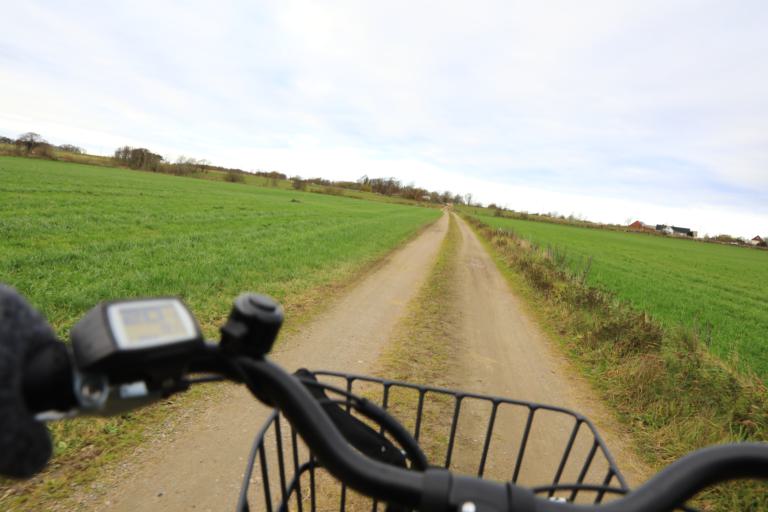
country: SE
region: Halland
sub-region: Varbergs Kommun
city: Traslovslage
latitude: 57.0591
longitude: 12.3279
